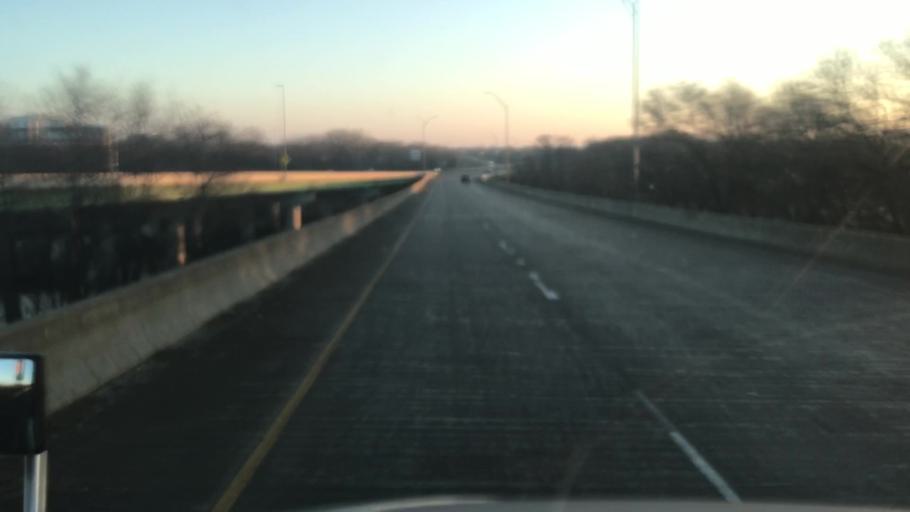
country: US
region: Iowa
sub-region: Black Hawk County
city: Evansdale
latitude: 42.4549
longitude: -92.3075
